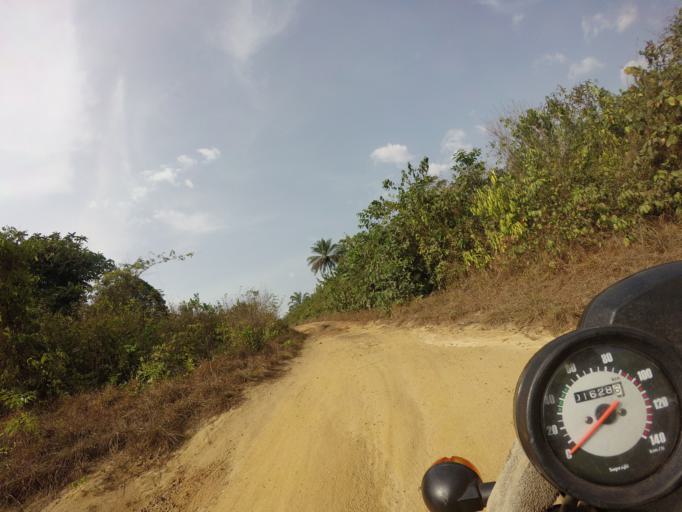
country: SL
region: Southern Province
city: Zimmi
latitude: 7.2198
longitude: -11.1816
